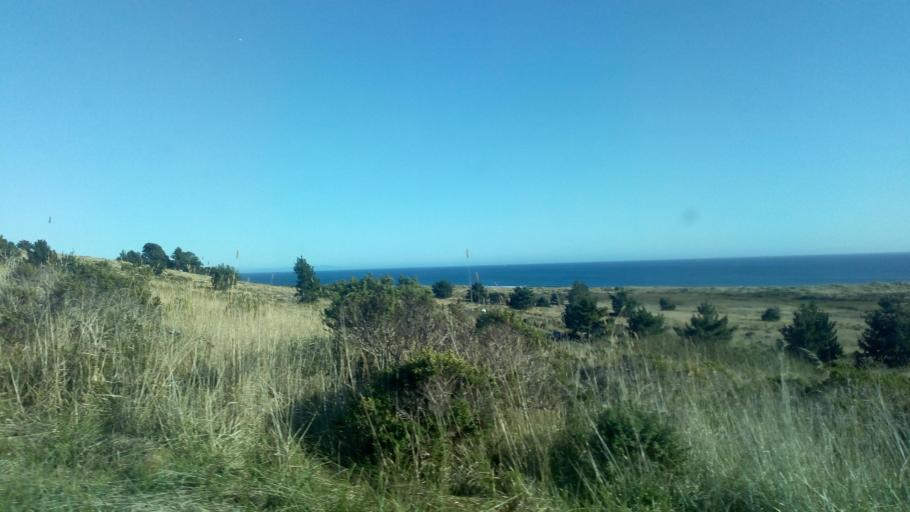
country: US
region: California
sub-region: Marin County
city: Inverness
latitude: 38.0309
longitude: -122.8812
